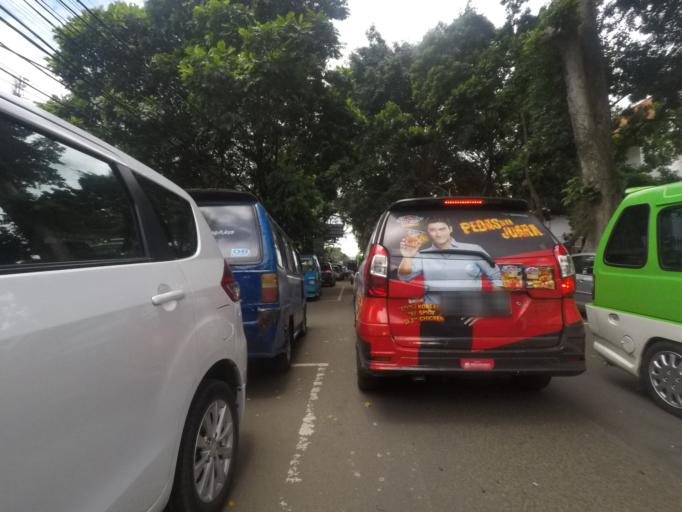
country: ID
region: West Java
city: Bogor
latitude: -6.5919
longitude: 106.7957
